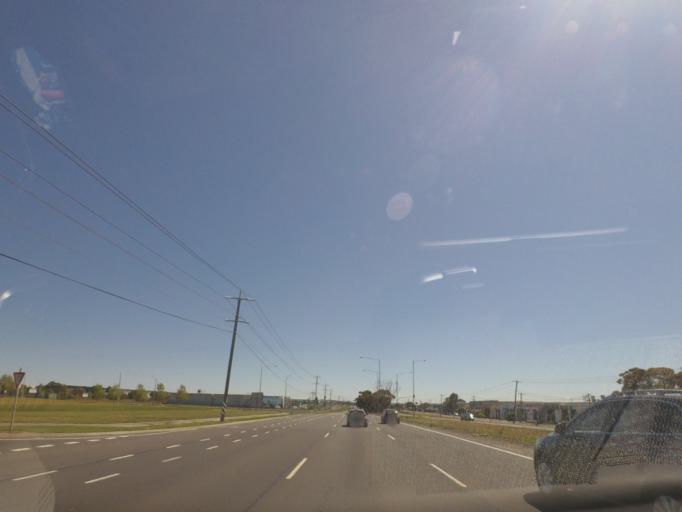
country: AU
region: Victoria
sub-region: Hume
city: Coolaroo
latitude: -37.6393
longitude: 144.9505
